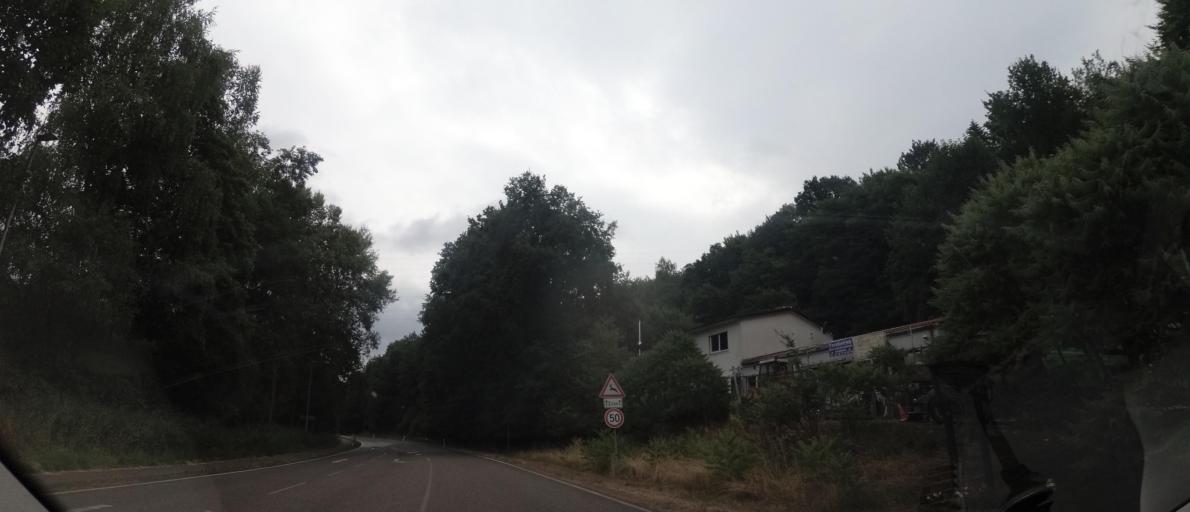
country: DE
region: Saarland
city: Sankt Ingbert
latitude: 49.2461
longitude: 7.1566
